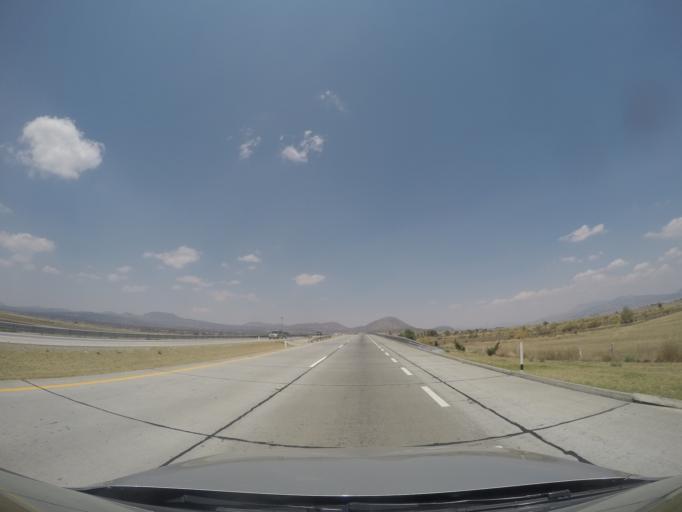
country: MX
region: Hidalgo
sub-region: Emiliano Zapata
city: Emiliano Zapata
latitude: 19.6348
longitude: -98.5600
